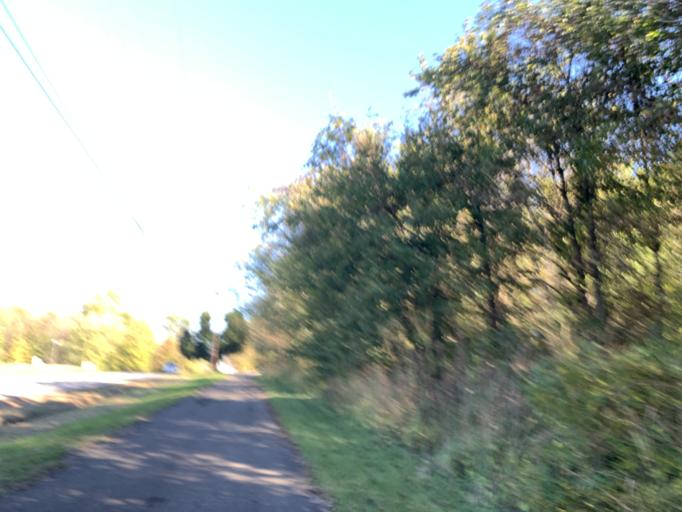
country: US
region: Kentucky
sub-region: Jefferson County
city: Pleasure Ridge Park
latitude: 38.1476
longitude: -85.8987
